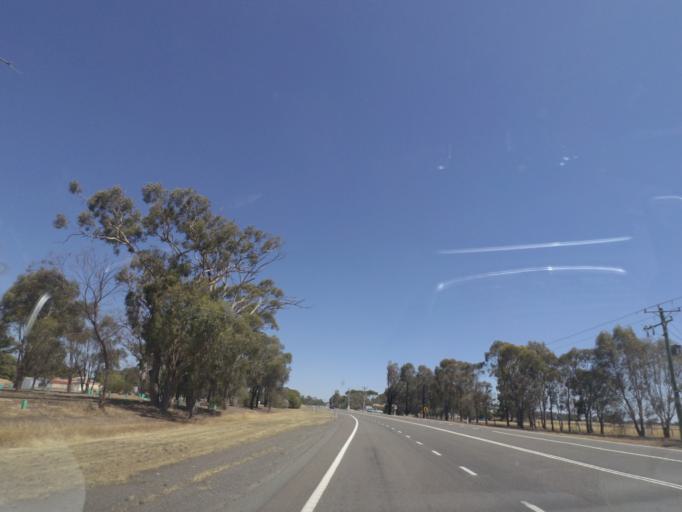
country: AU
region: Victoria
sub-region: Greater Shepparton
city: Shepparton
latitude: -36.2369
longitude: 145.4315
